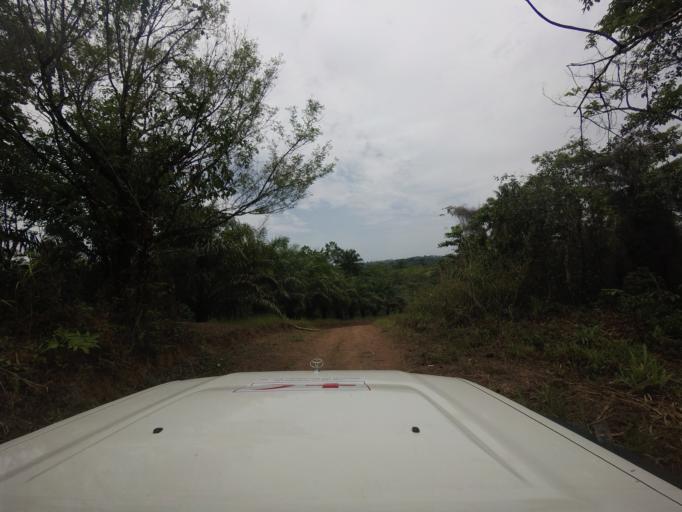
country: SL
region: Eastern Province
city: Buedu
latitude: 8.2476
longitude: -10.2927
